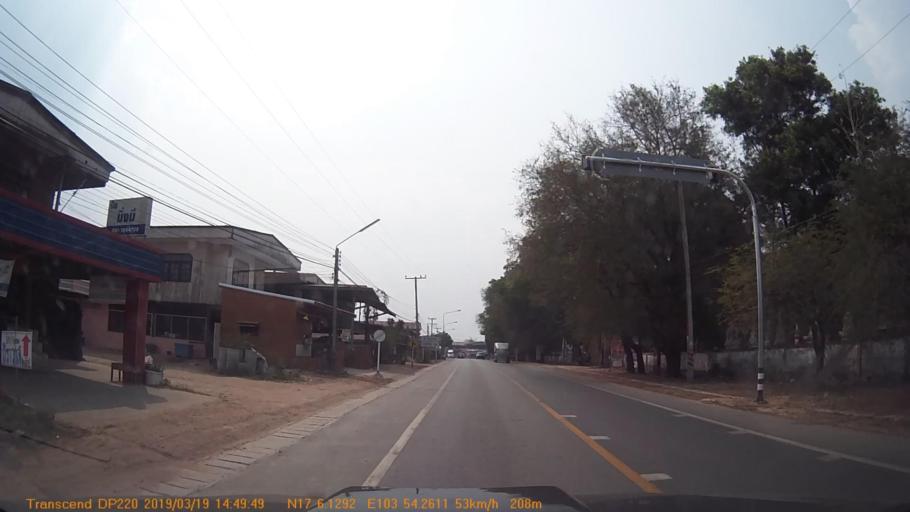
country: TH
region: Sakon Nakhon
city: Kut Bak
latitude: 17.1022
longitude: 103.9041
